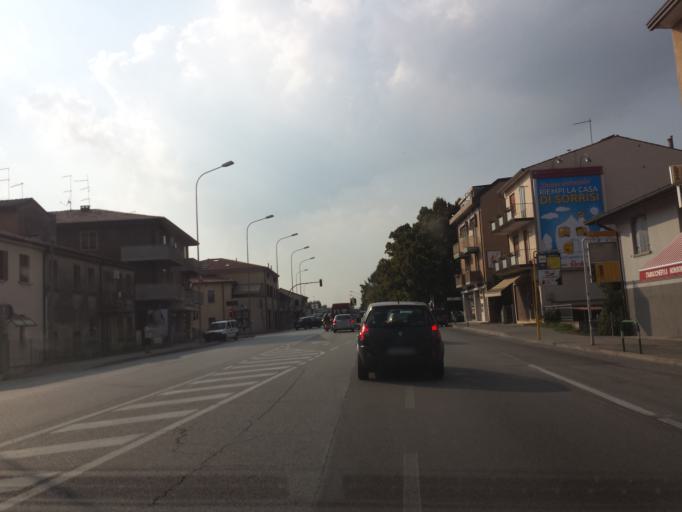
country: IT
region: Veneto
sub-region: Provincia di Padova
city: Caselle
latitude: 45.4167
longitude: 11.8293
